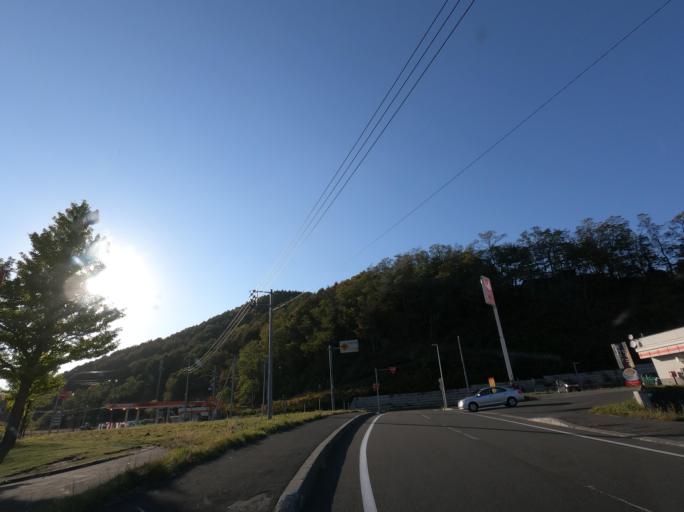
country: JP
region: Hokkaido
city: Iwamizawa
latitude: 43.0522
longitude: 141.9687
